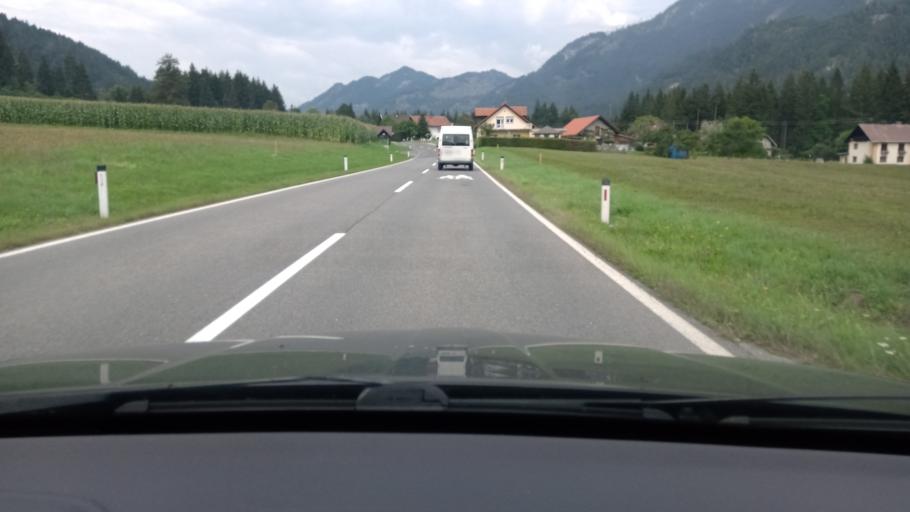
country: AT
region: Carinthia
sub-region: Politischer Bezirk Hermagor
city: Hermagor
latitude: 46.6440
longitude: 13.3379
